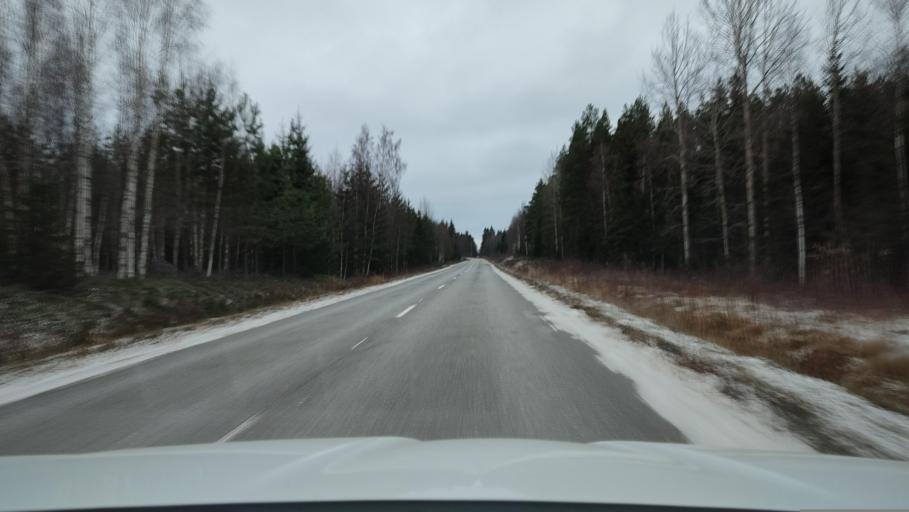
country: FI
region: Ostrobothnia
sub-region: Vaasa
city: Replot
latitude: 63.2613
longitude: 21.3618
